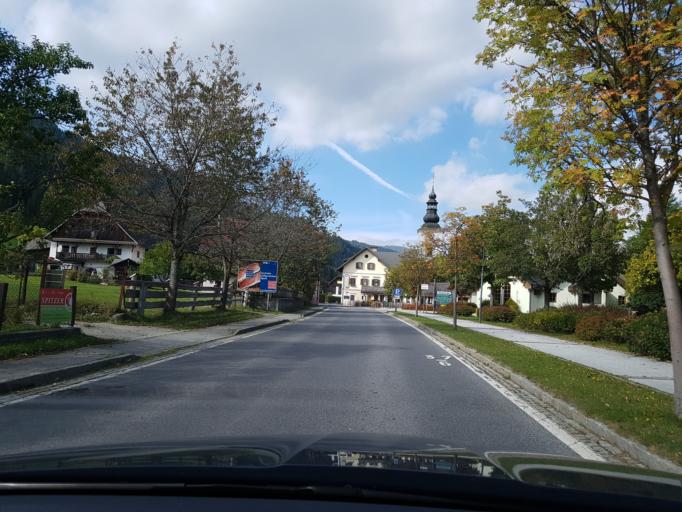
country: AT
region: Carinthia
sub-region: Politischer Bezirk Feldkirchen
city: Gnesau
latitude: 46.7748
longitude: 13.9665
